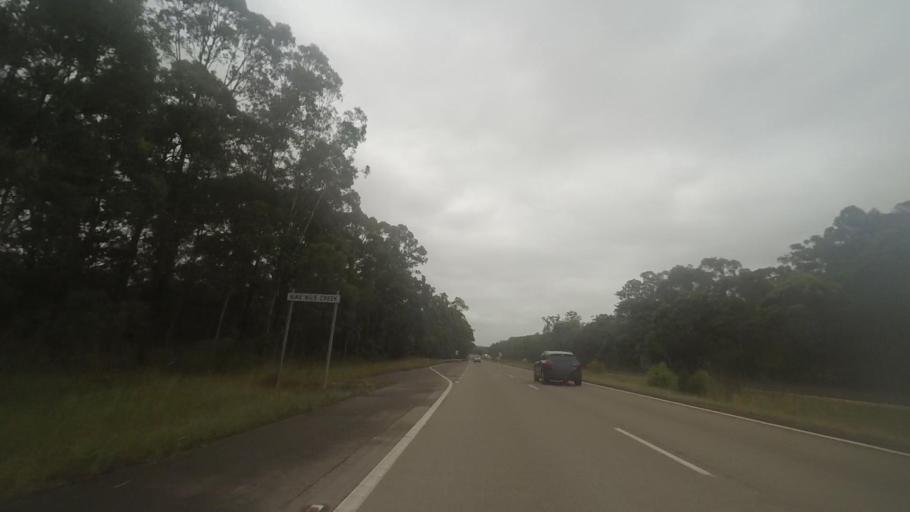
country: AU
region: New South Wales
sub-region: Port Stephens Shire
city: Medowie
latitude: -32.6737
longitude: 151.8274
